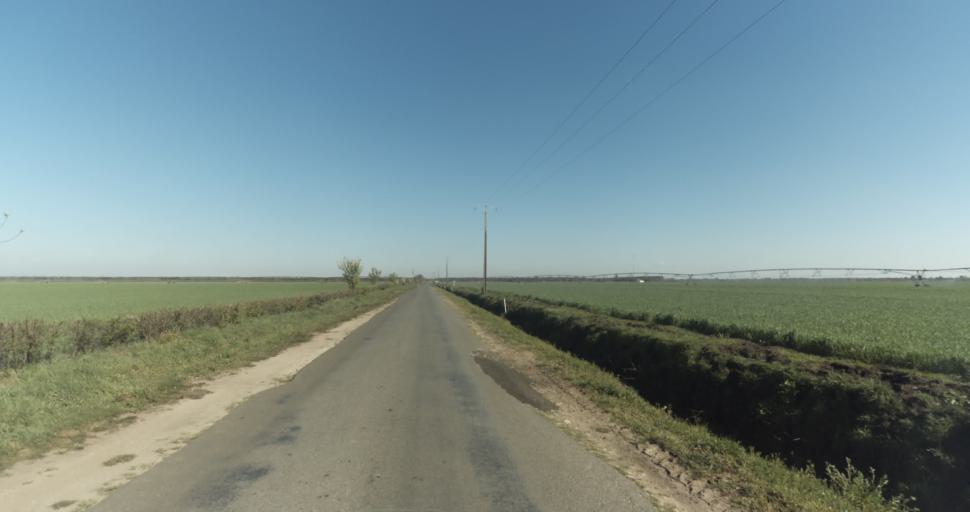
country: FR
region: Aquitaine
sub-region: Departement de la Gironde
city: Marcheprime
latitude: 44.7661
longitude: -0.8547
